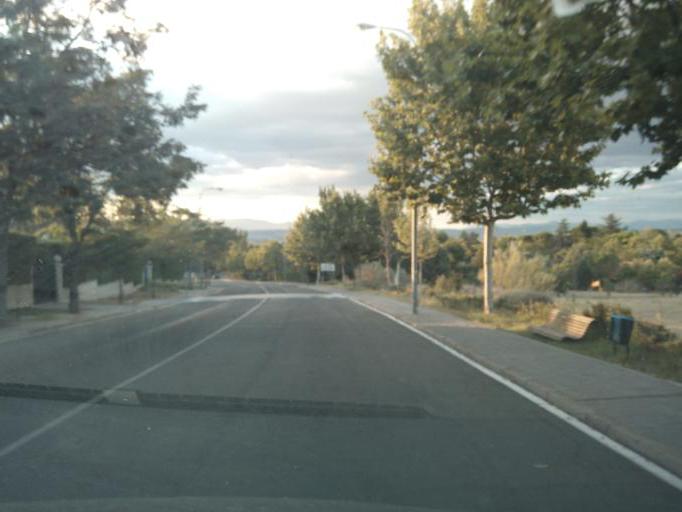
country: ES
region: Madrid
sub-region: Provincia de Madrid
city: Valdeolmos
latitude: 40.6143
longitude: -3.4708
